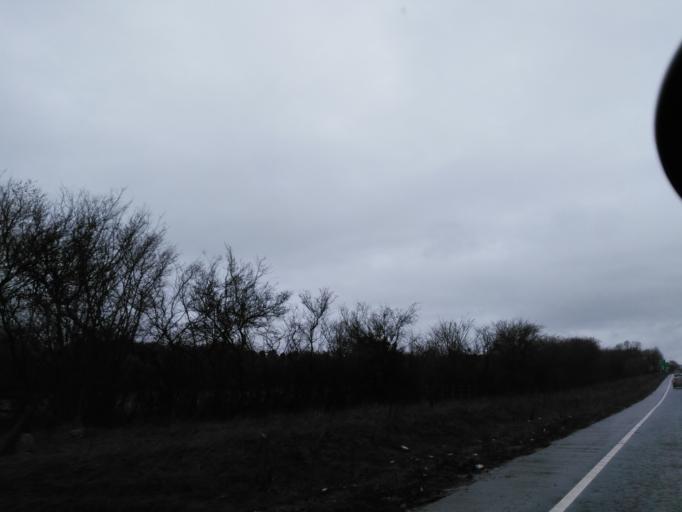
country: GB
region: England
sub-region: Wiltshire
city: Chippenham
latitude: 51.4854
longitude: -2.1287
